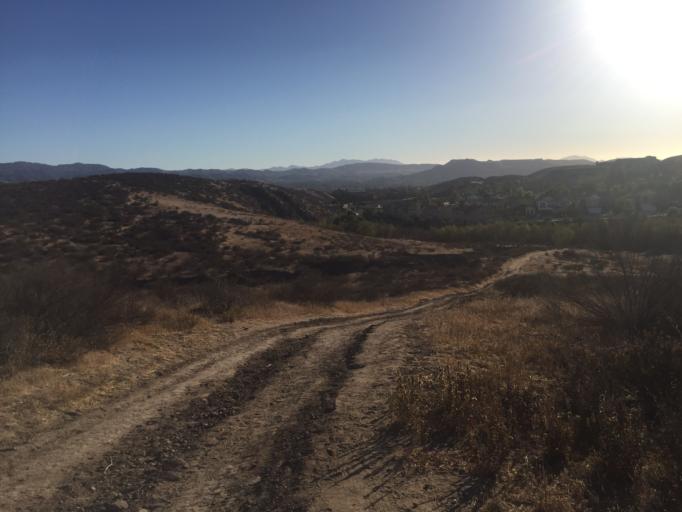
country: US
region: California
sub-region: Ventura County
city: Simi Valley
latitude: 34.2921
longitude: -118.7594
